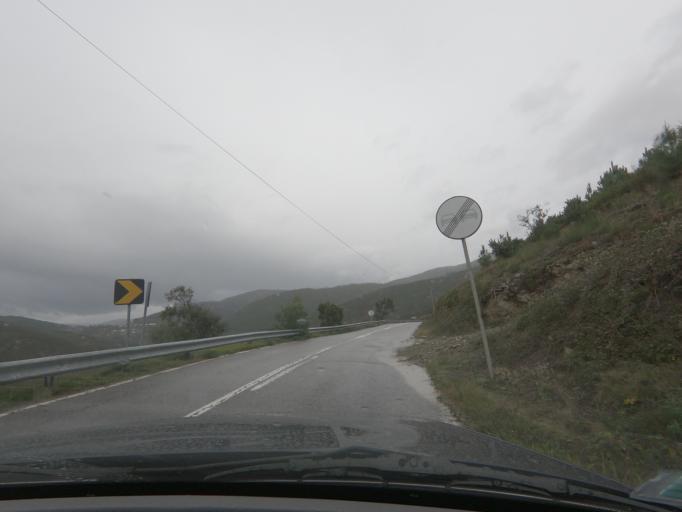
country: PT
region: Vila Real
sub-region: Mondim de Basto
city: Mondim de Basto
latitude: 41.3522
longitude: -7.9180
